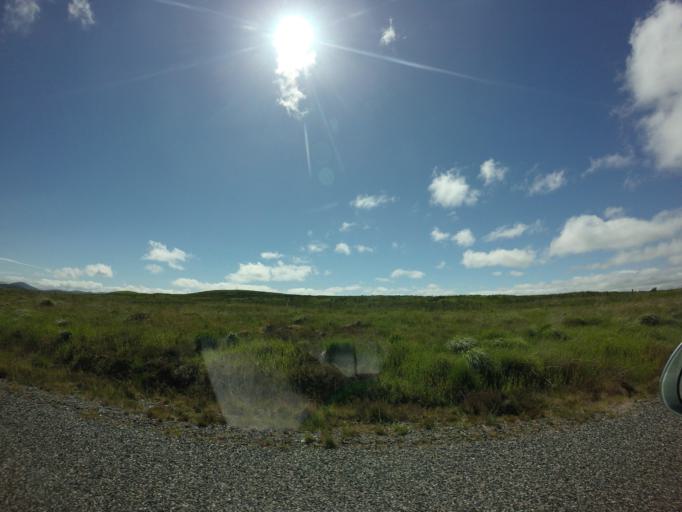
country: GB
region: Scotland
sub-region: Eilean Siar
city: Harris
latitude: 58.1945
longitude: -6.7167
